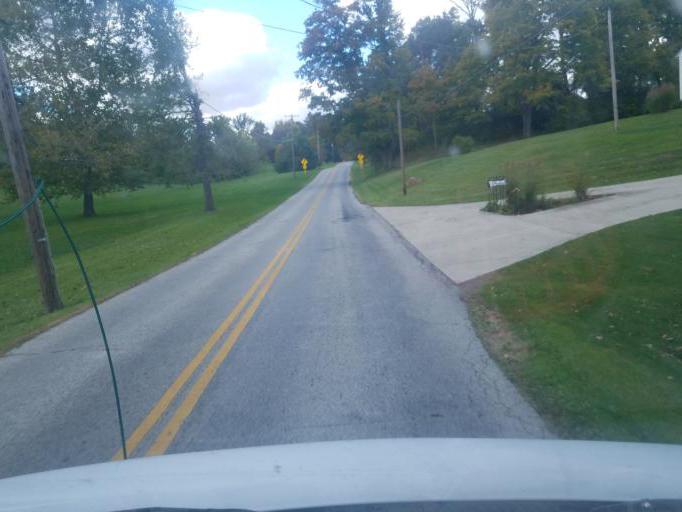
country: US
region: Ohio
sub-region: Richland County
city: Ontario
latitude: 40.7330
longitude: -82.5772
